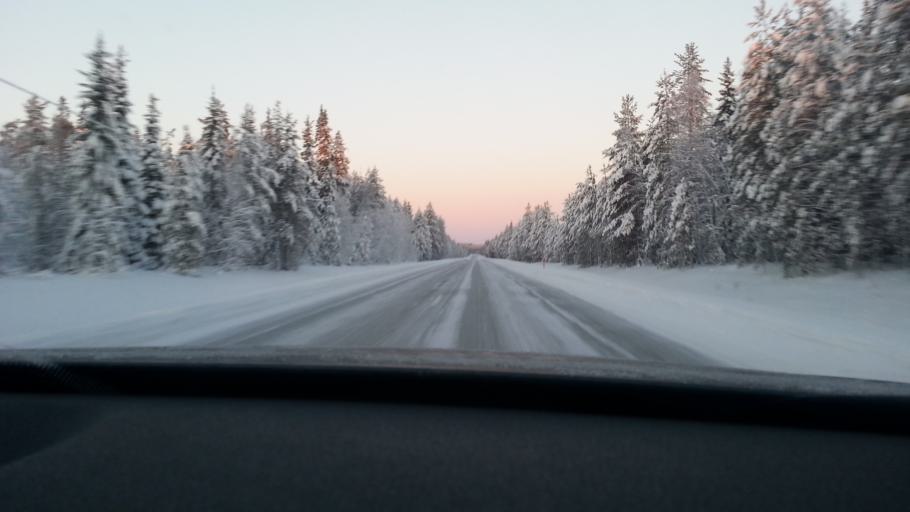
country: FI
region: Lapland
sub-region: Tunturi-Lappi
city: Kittilae
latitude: 67.2212
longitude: 24.9237
